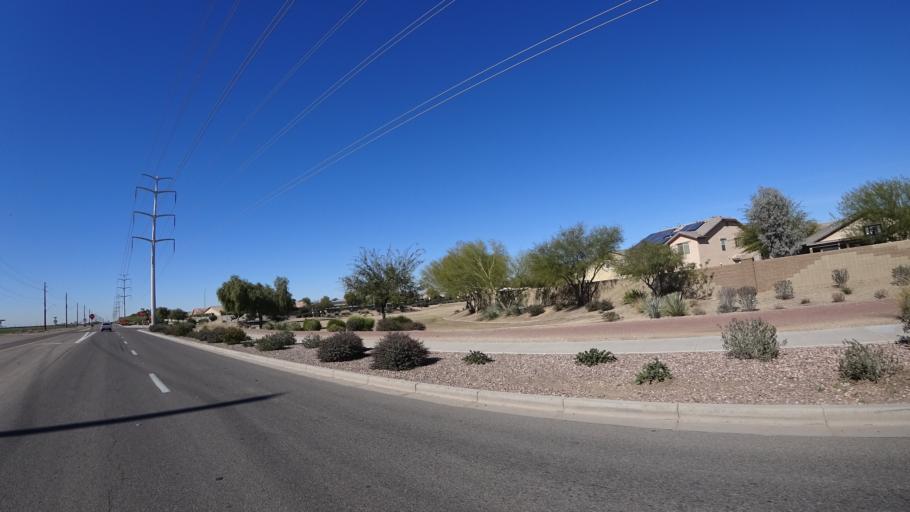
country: US
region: Arizona
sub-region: Maricopa County
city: Tolleson
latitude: 33.4085
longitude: -112.2201
